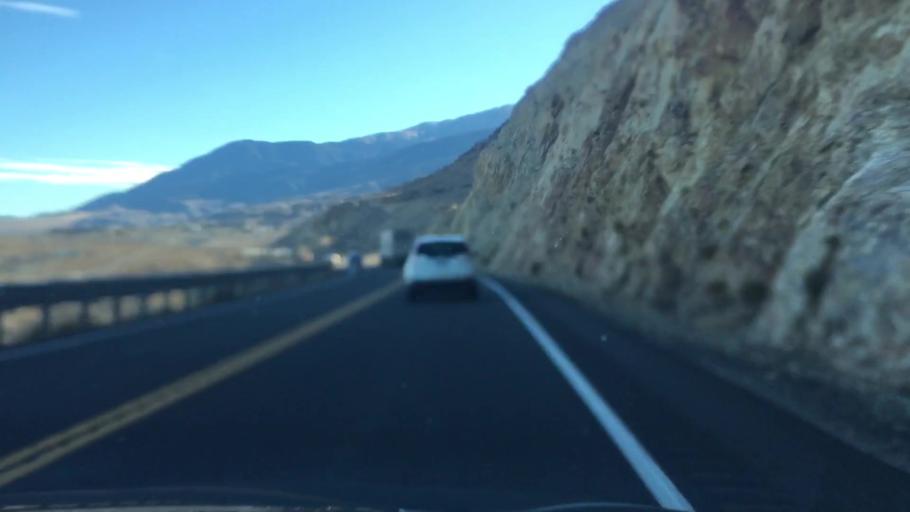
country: US
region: Nevada
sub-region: Mineral County
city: Hawthorne
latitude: 38.6667
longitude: -118.7675
